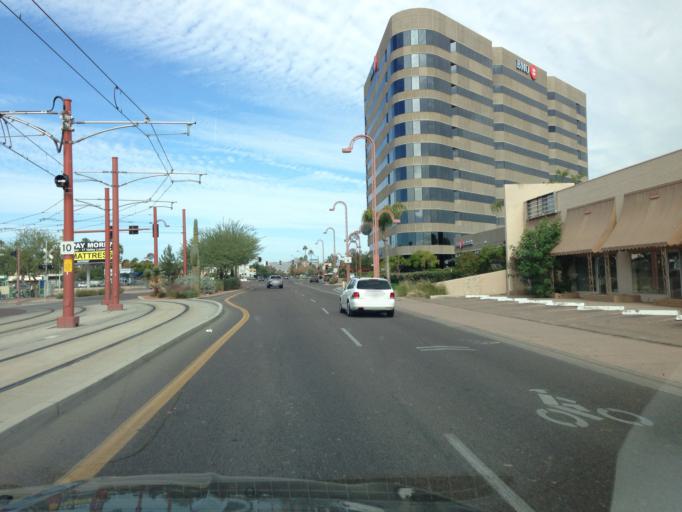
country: US
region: Arizona
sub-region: Maricopa County
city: Phoenix
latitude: 33.5074
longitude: -112.0737
